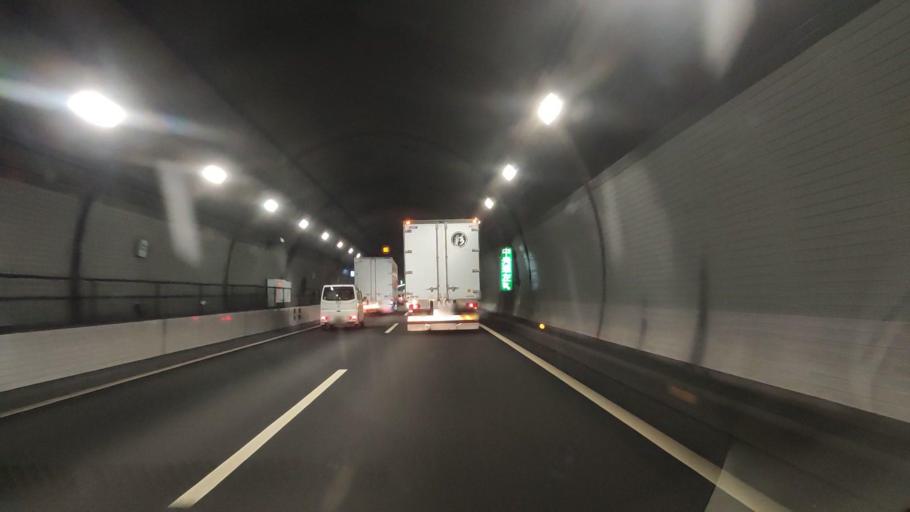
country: JP
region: Tokyo
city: Hachioji
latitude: 35.6461
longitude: 139.2524
